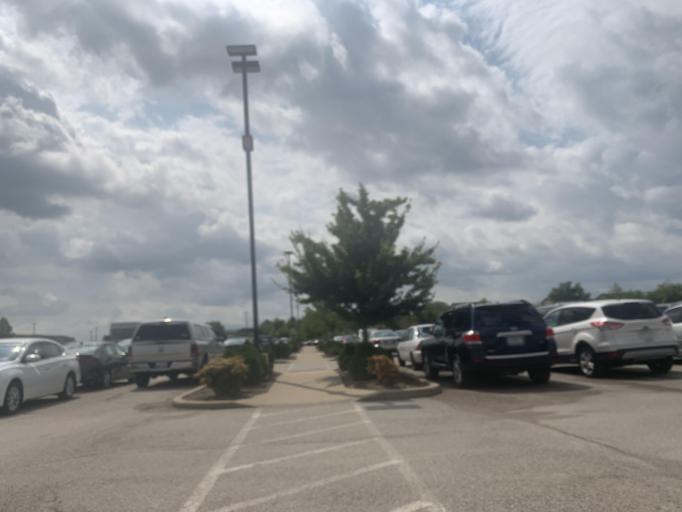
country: US
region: Kentucky
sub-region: Jefferson County
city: Louisville
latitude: 38.2227
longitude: -85.7651
